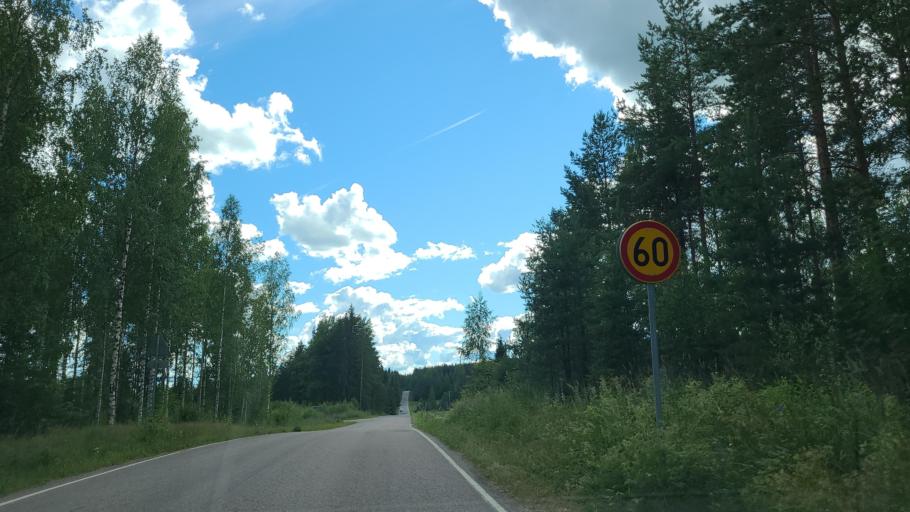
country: FI
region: Central Finland
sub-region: Jaemsae
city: Jaemsae
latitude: 61.8951
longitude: 25.2614
